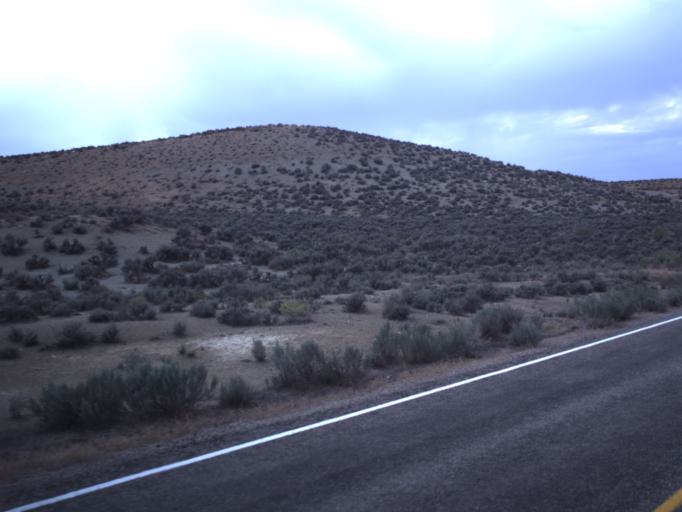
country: US
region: Colorado
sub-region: Rio Blanco County
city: Rangely
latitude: 40.0385
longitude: -109.1849
